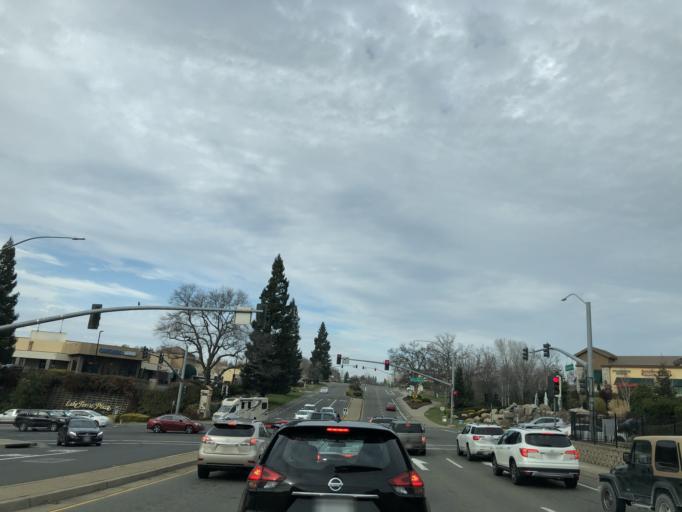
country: US
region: California
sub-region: El Dorado County
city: El Dorado Hills
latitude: 38.7090
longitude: -121.0851
